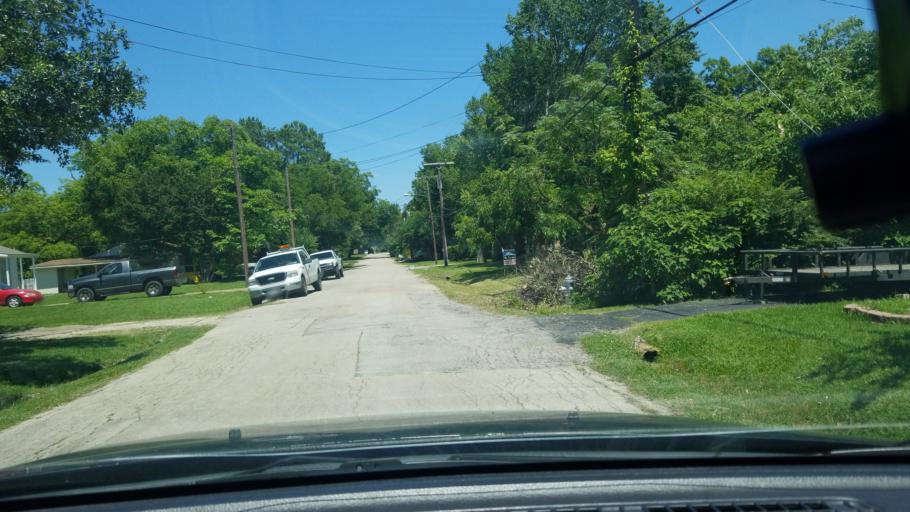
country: US
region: Texas
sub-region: Dallas County
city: Mesquite
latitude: 32.7641
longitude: -96.6067
